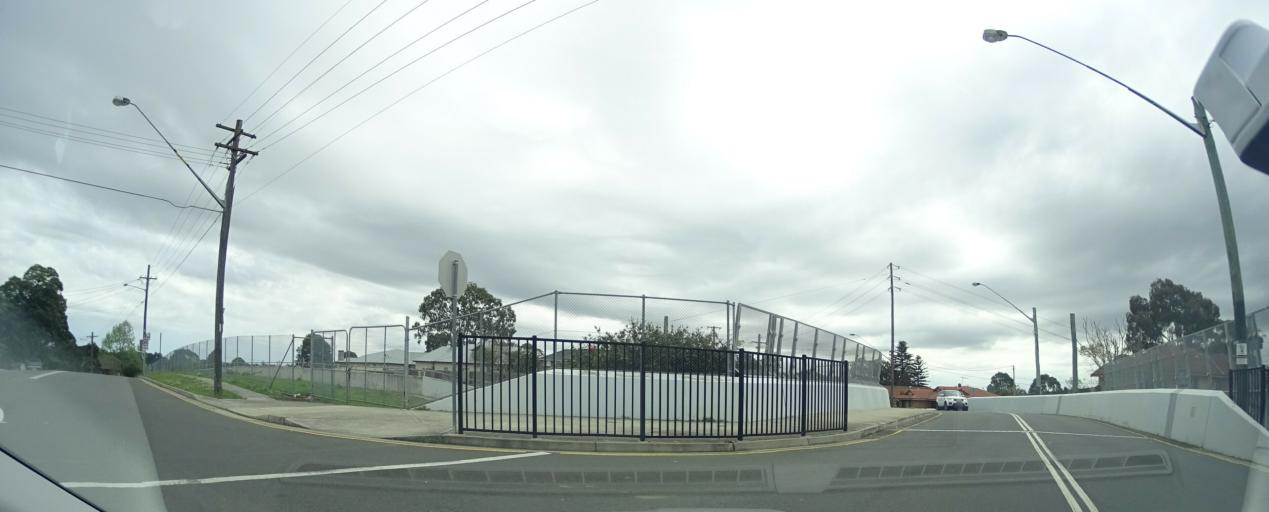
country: AU
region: New South Wales
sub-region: Bankstown
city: Padstow
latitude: -33.9524
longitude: 151.0264
